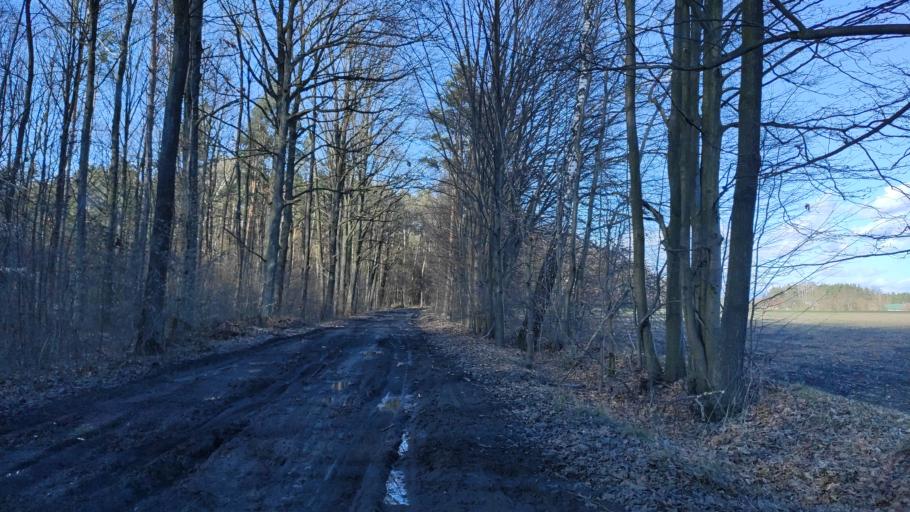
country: PL
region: Masovian Voivodeship
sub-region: Powiat radomski
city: Jedlnia-Letnisko
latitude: 51.4569
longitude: 21.3242
